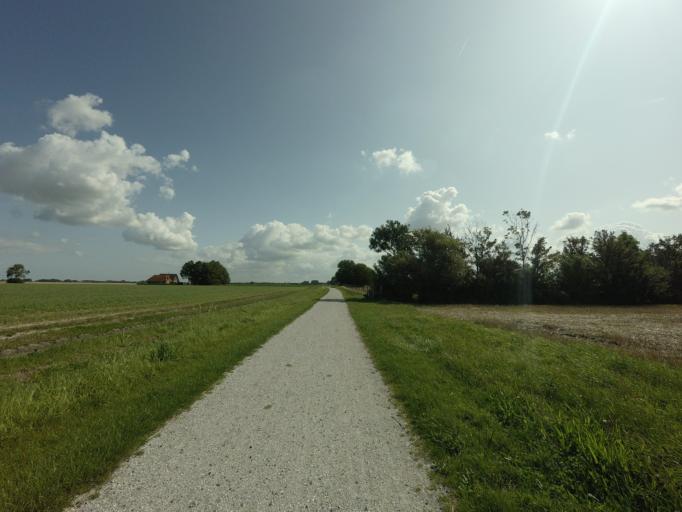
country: NL
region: Friesland
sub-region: Gemeente Het Bildt
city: Sint Annaparochie
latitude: 53.2801
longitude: 5.6734
